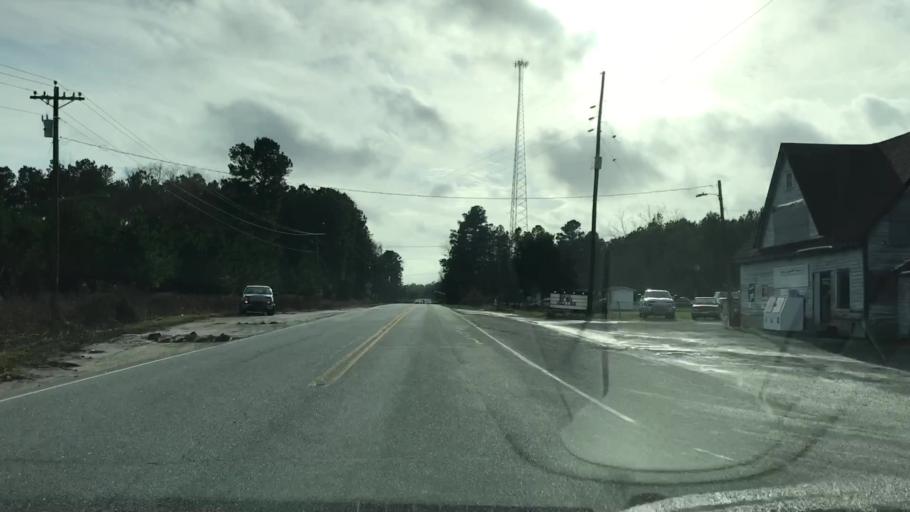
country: US
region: South Carolina
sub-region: Williamsburg County
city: Andrews
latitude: 33.3583
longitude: -79.6559
